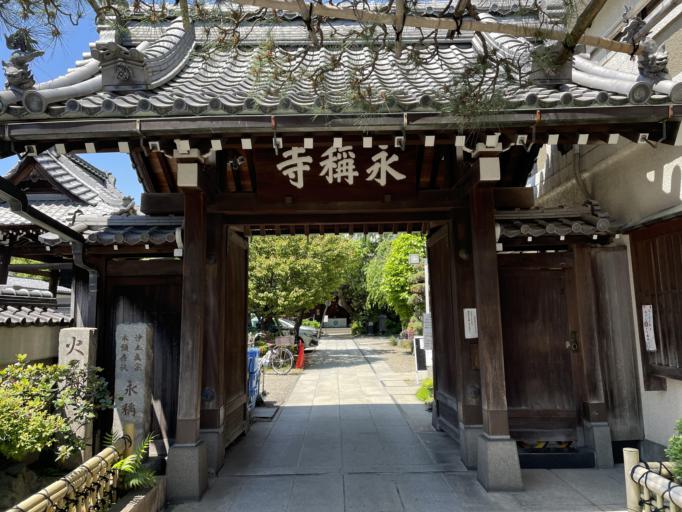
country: JP
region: Tokyo
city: Tokyo
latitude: 35.7231
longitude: 139.7819
